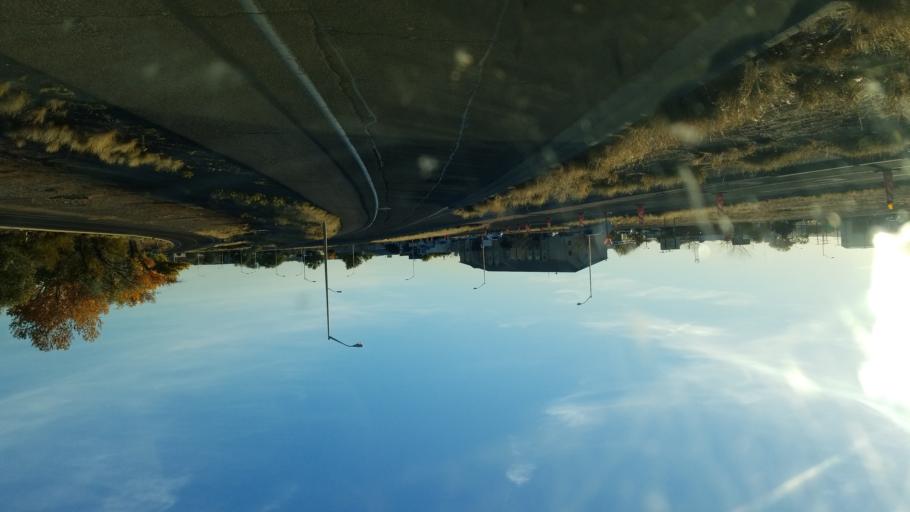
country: US
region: New Mexico
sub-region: San Juan County
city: Farmington
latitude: 36.7201
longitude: -108.1828
